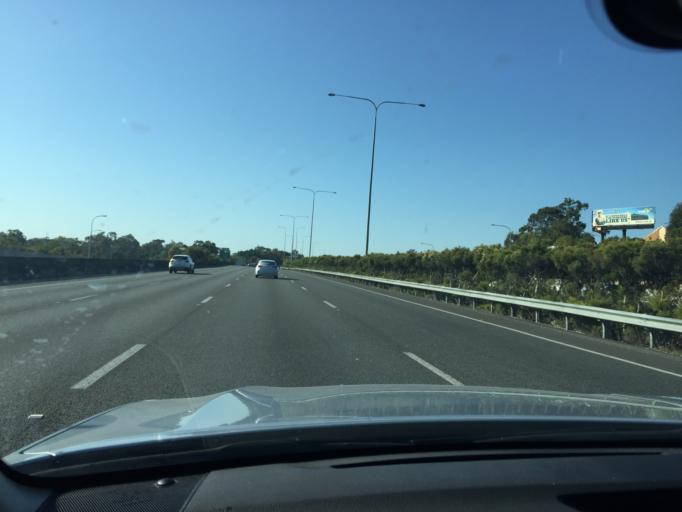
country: AU
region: Queensland
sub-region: Logan
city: Beenleigh
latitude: -27.7037
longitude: 153.2011
